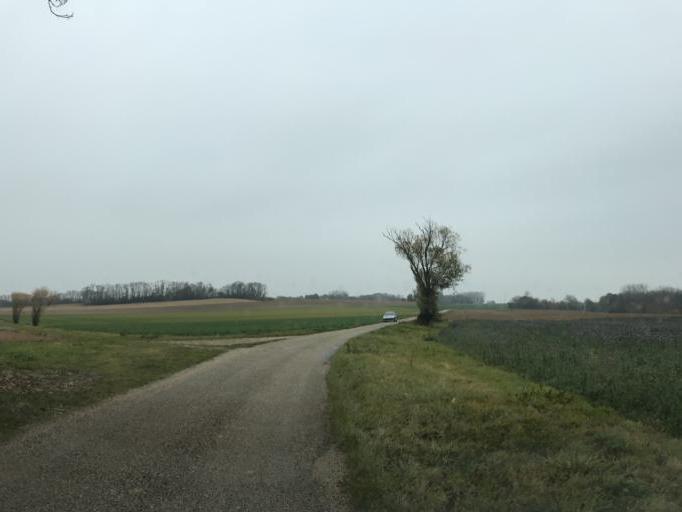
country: FR
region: Rhone-Alpes
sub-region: Departement de l'Ain
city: Saint-Maurice-de-Beynost
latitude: 45.8411
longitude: 4.9689
